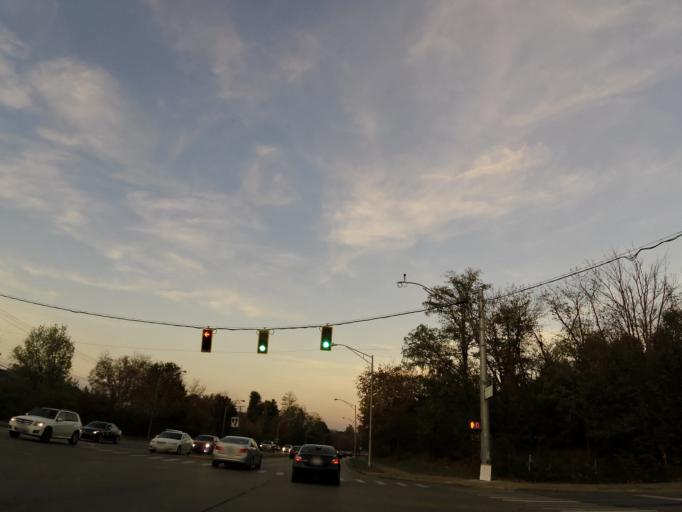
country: US
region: Kentucky
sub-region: Fayette County
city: Lexington
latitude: 37.9902
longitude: -84.4568
